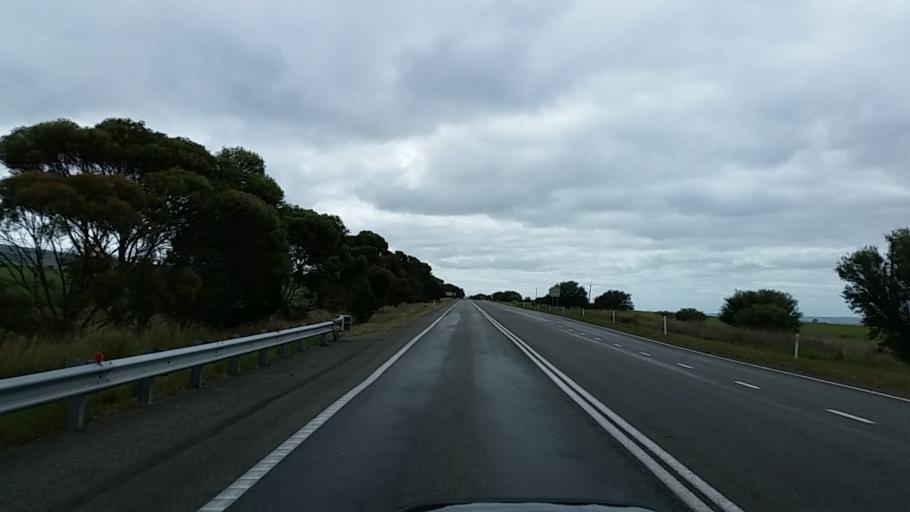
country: AU
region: South Australia
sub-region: Port Pirie City and Dists
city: Crystal Brook
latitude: -33.7184
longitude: 138.2111
